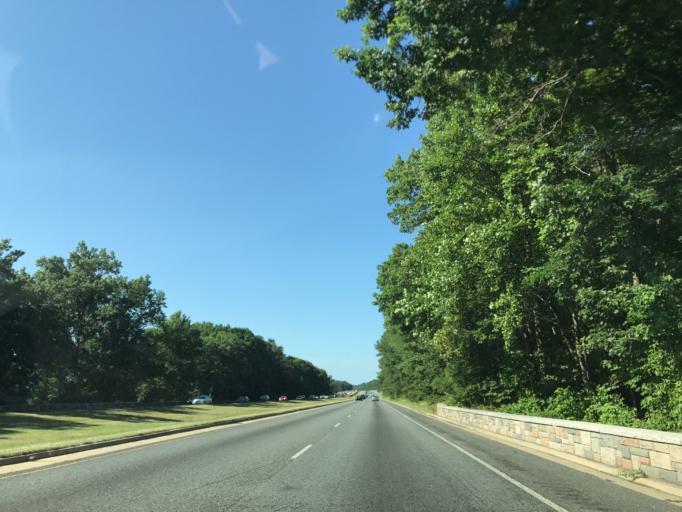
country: US
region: Maryland
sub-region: Prince George's County
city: South Laurel
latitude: 39.0409
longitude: -76.8483
